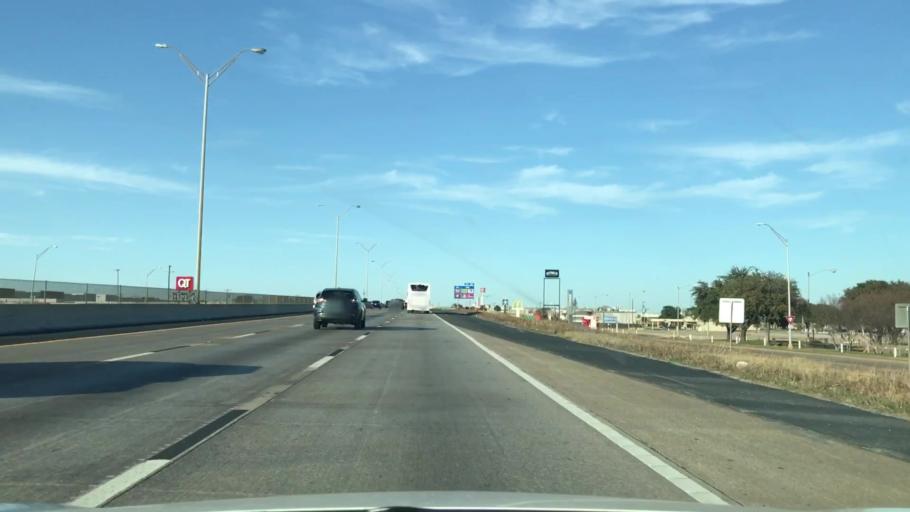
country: US
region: Texas
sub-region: Tarrant County
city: Everman
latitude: 32.6242
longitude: -97.3215
